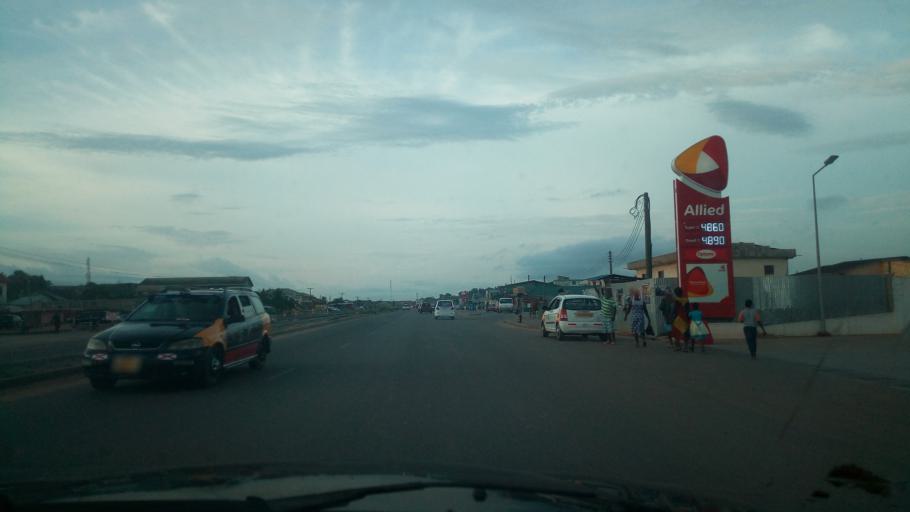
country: GH
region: Western
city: Takoradi
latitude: 4.9233
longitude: -1.7841
